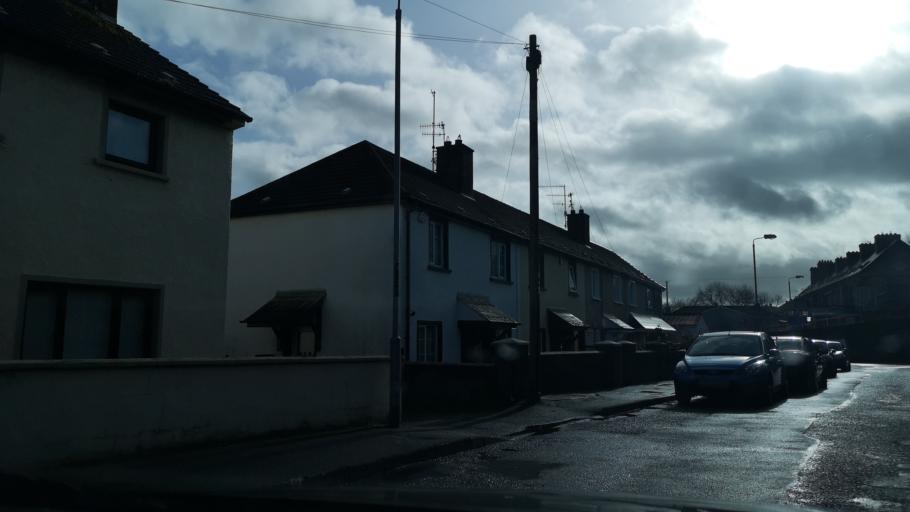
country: GB
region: Northern Ireland
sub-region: Newry and Mourne District
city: Newry
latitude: 54.1827
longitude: -6.3501
